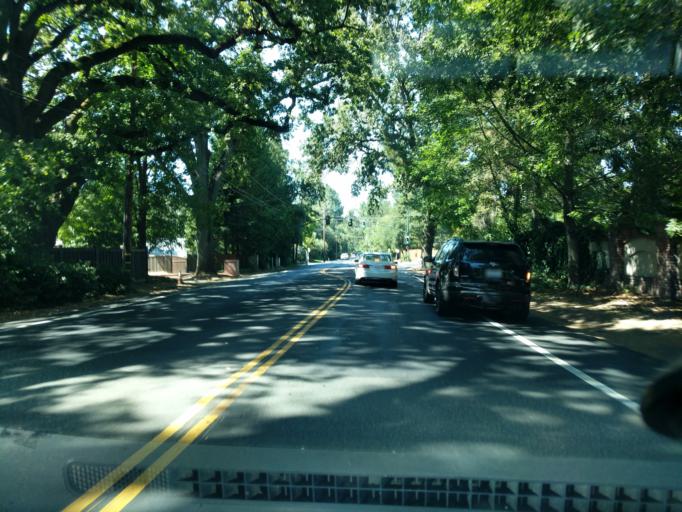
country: US
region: California
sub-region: Contra Costa County
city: Alamo
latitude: 37.8610
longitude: -122.0394
